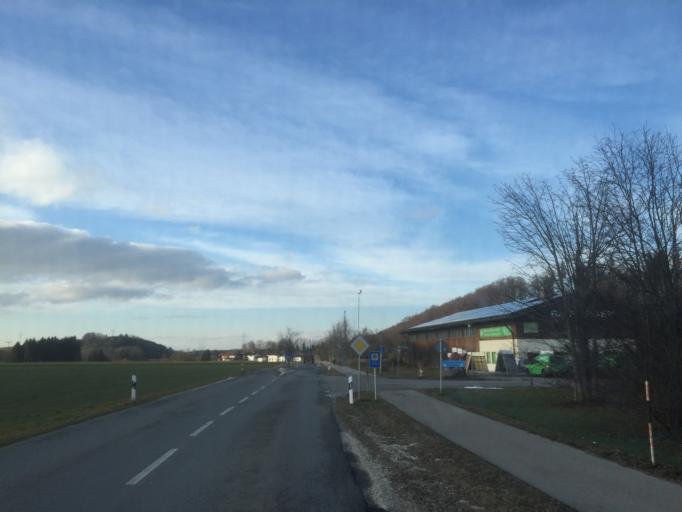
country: DE
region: Bavaria
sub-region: Upper Bavaria
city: Vachendorf
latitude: 47.8458
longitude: 12.6030
